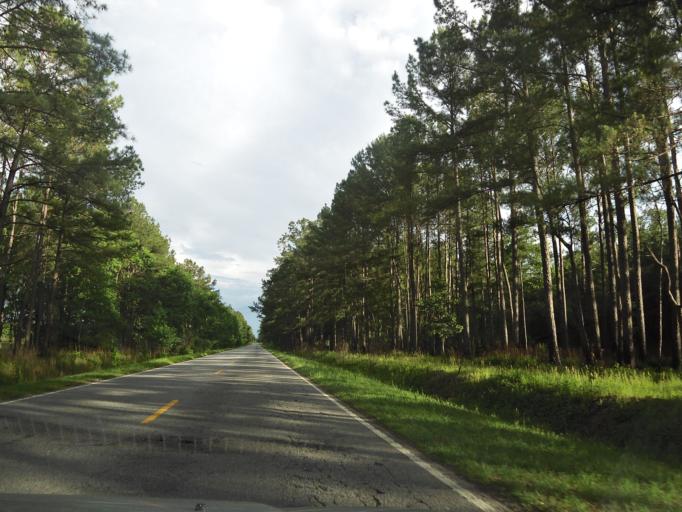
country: US
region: South Carolina
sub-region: Jasper County
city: Ridgeland
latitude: 32.5437
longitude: -81.1615
